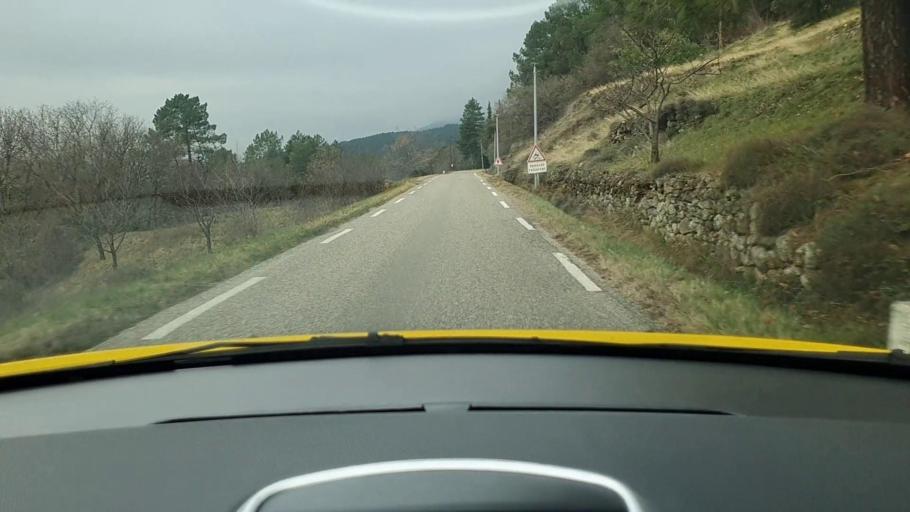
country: FR
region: Languedoc-Roussillon
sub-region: Departement du Gard
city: Besseges
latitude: 44.3171
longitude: 4.0711
